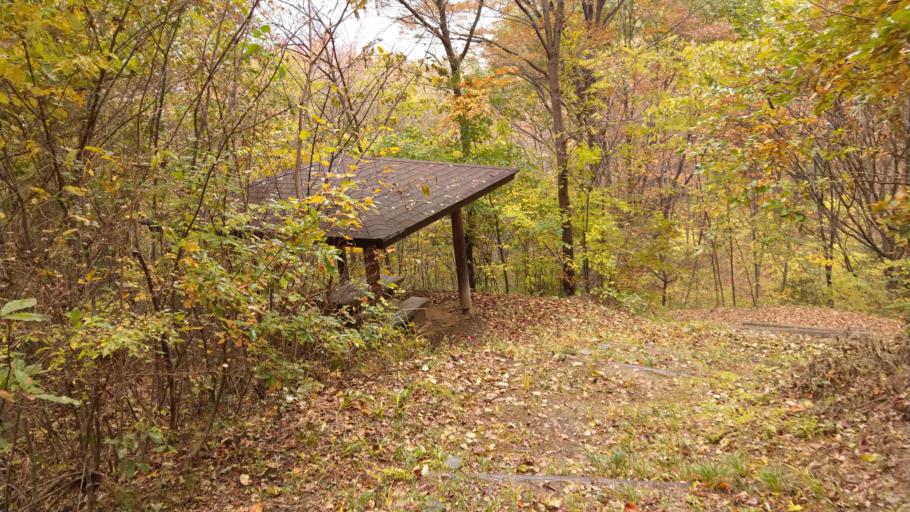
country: JP
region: Nagano
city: Komoro
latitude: 36.3096
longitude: 138.4351
